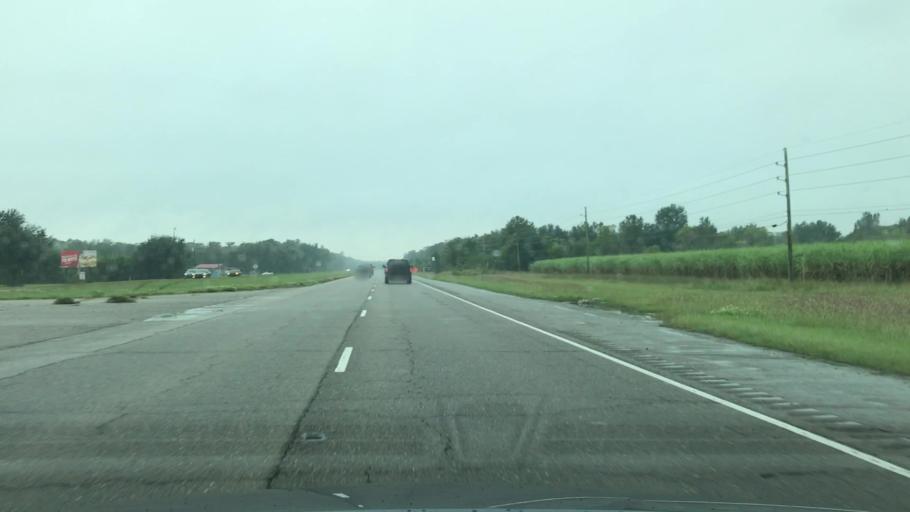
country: US
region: Louisiana
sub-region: Lafourche Parish
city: Raceland
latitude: 29.7397
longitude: -90.5574
